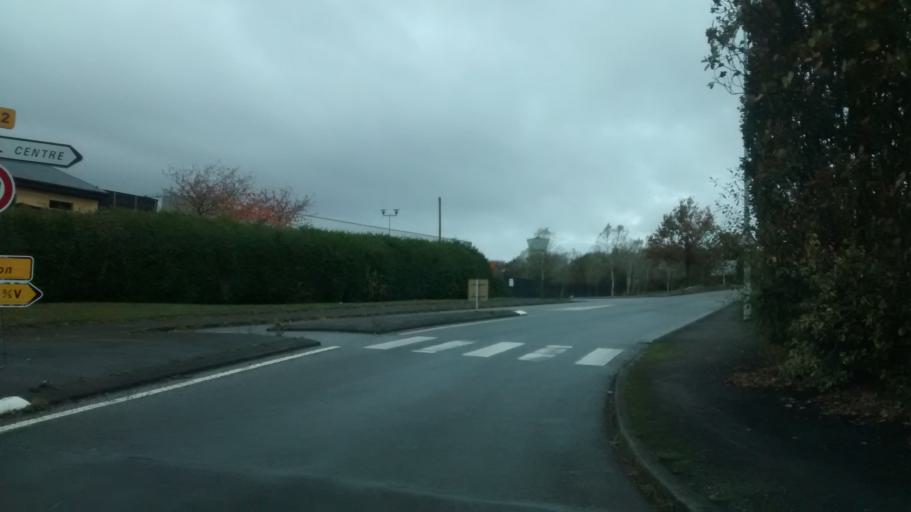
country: FR
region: Brittany
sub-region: Departement d'Ille-et-Vilaine
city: Noyal-sur-Vilaine
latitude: 48.1063
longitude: -1.5211
